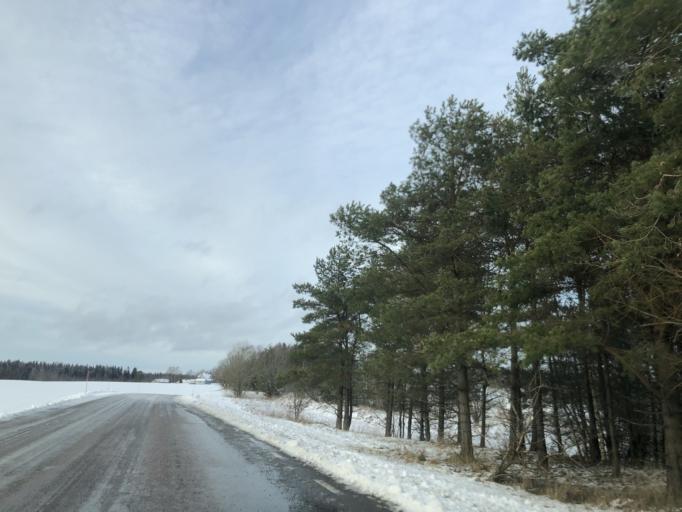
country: SE
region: Vaestra Goetaland
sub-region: Ulricehamns Kommun
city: Ulricehamn
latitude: 57.8140
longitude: 13.5352
